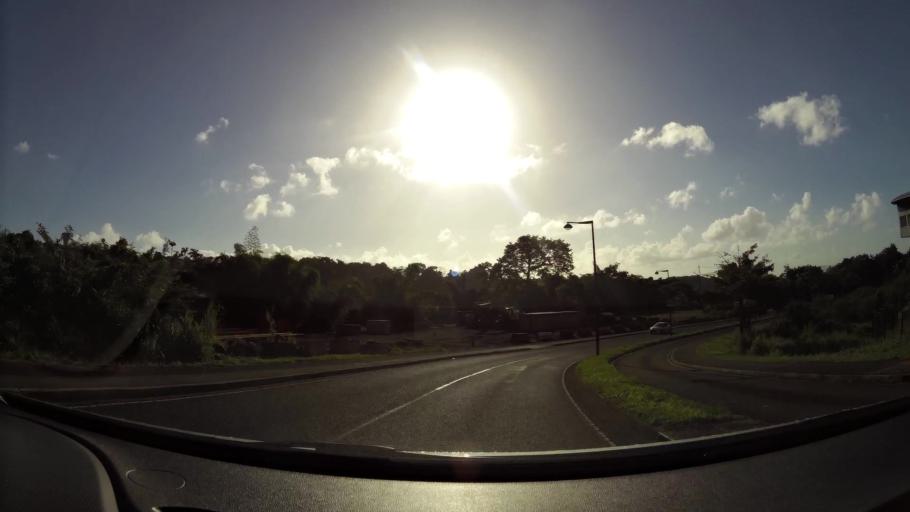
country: MQ
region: Martinique
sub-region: Martinique
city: Saint-Joseph
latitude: 14.6348
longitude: -61.0359
